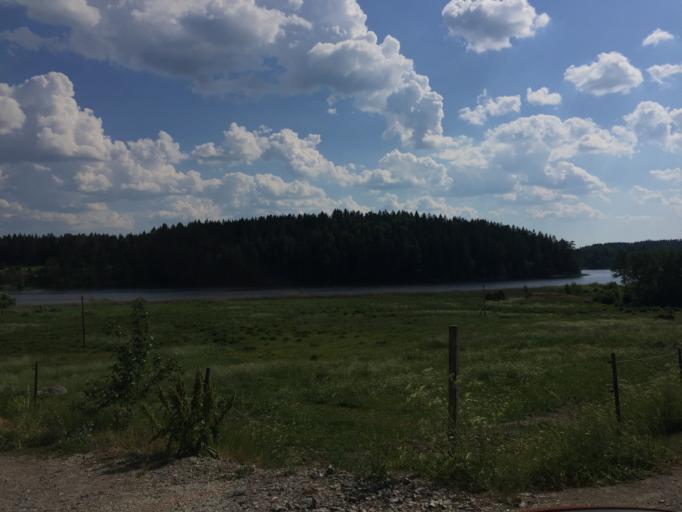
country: SE
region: Soedermanland
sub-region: Flens Kommun
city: Halleforsnas
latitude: 59.0733
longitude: 16.4569
